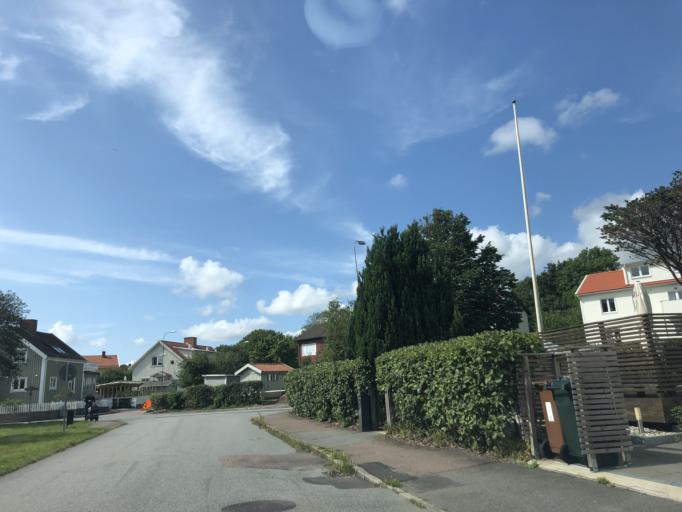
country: SE
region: Vaestra Goetaland
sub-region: Goteborg
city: Majorna
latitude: 57.7087
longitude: 11.9115
